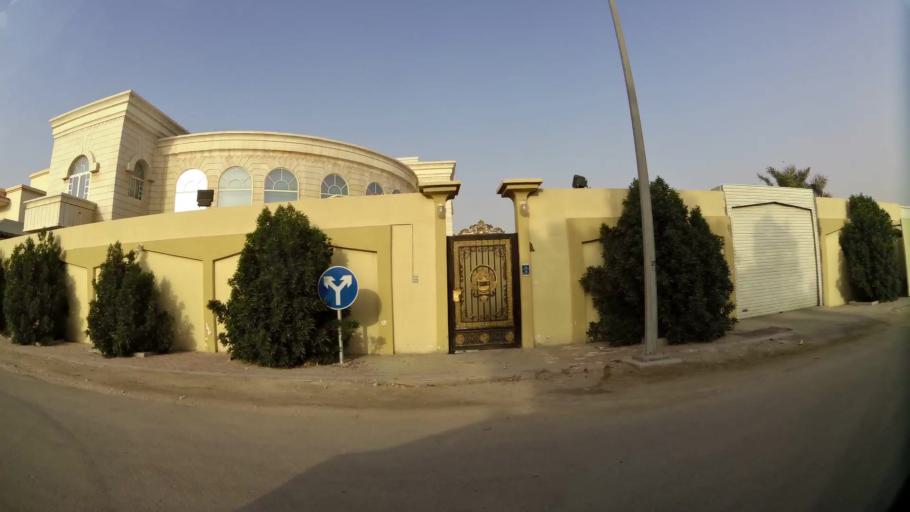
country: QA
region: Baladiyat ar Rayyan
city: Ar Rayyan
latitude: 25.2488
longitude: 51.4480
